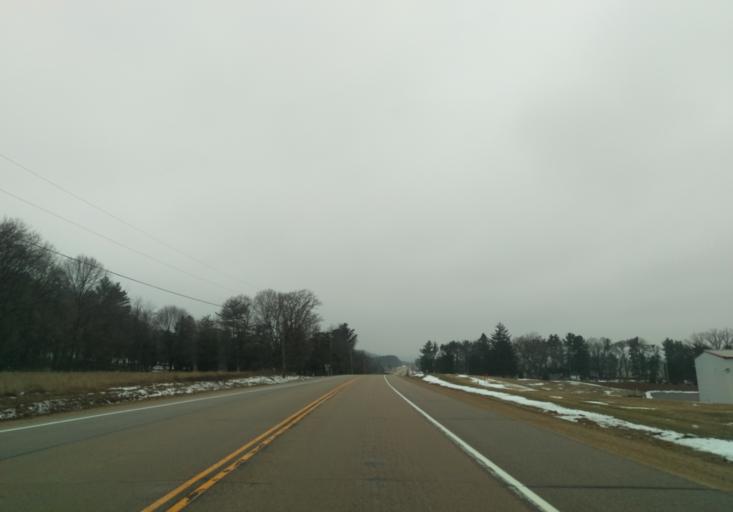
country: US
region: Wisconsin
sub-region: Dane County
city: Mazomanie
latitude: 43.1682
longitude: -89.8109
